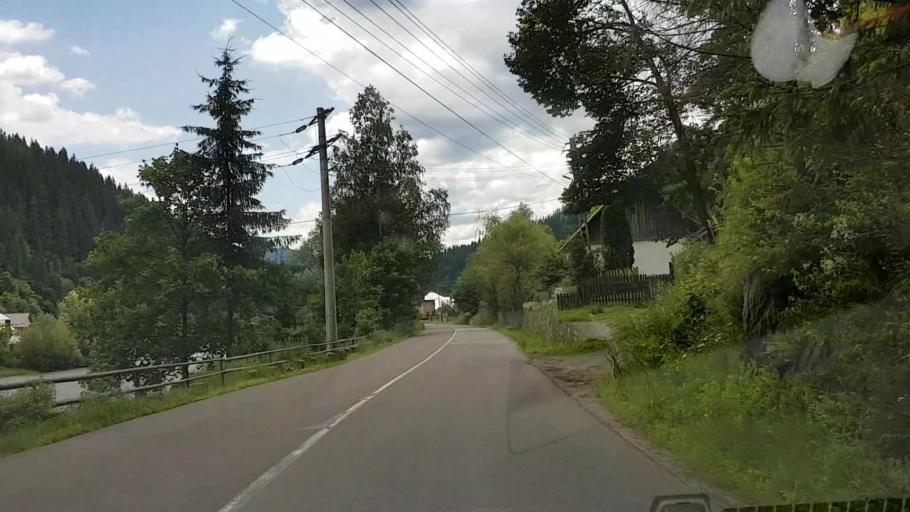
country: RO
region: Suceava
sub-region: Comuna Crucea
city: Crucea
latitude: 47.3462
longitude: 25.6074
